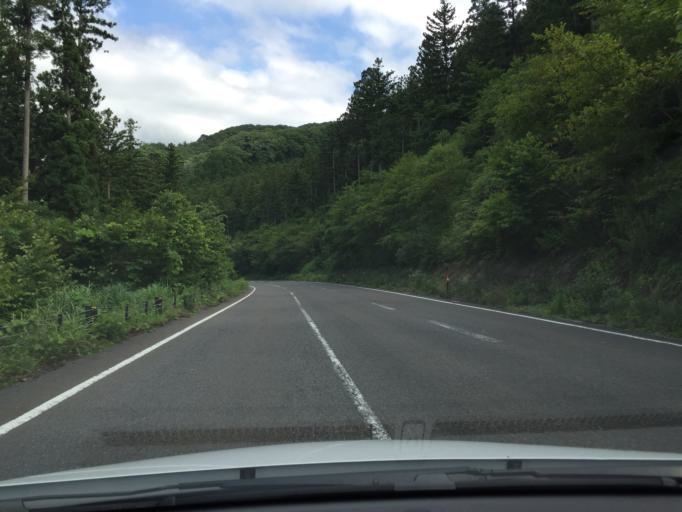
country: JP
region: Tochigi
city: Kuroiso
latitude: 37.2058
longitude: 140.1008
